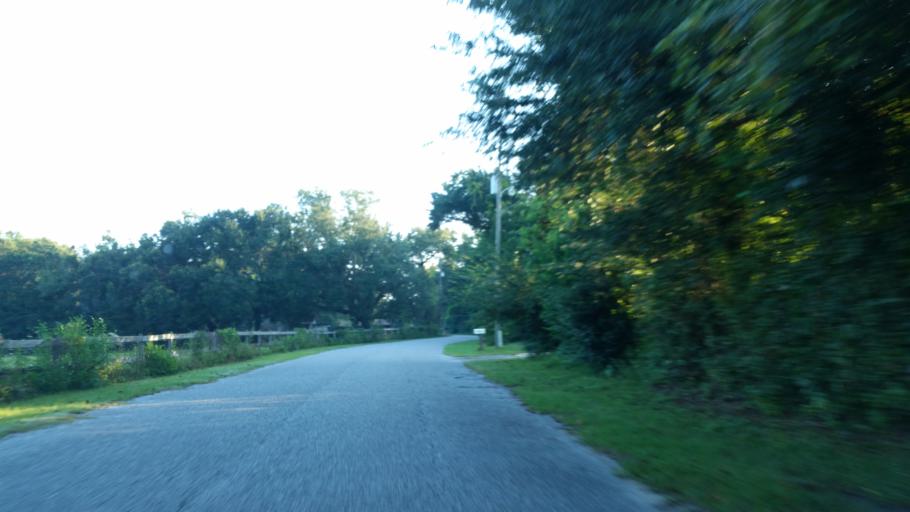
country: US
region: Florida
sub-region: Escambia County
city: Ferry Pass
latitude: 30.5314
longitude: -87.2028
